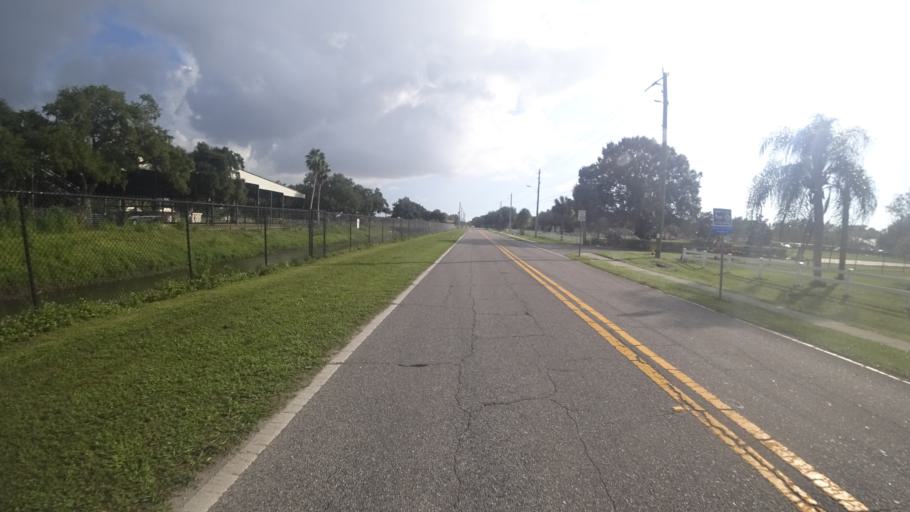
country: US
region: Florida
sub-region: Manatee County
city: Palmetto
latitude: 27.5273
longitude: -82.5812
